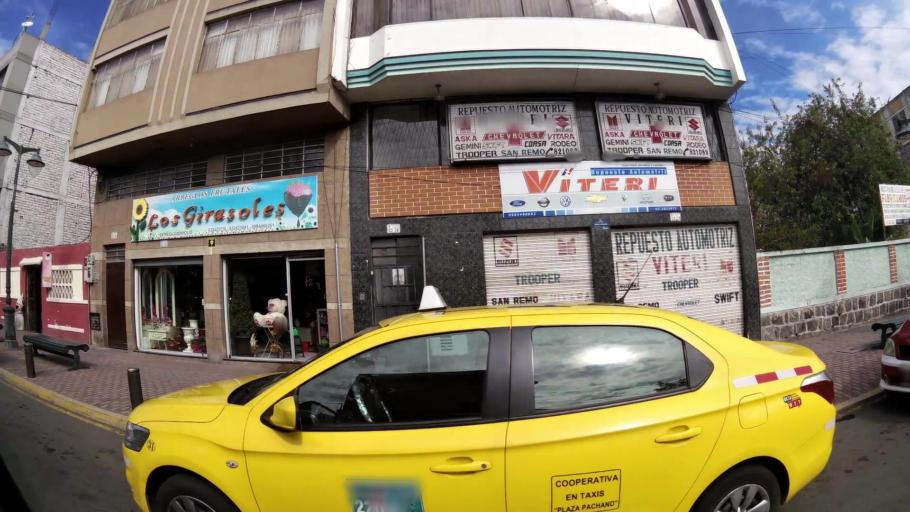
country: EC
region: Tungurahua
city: Ambato
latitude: -1.2324
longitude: -78.6303
